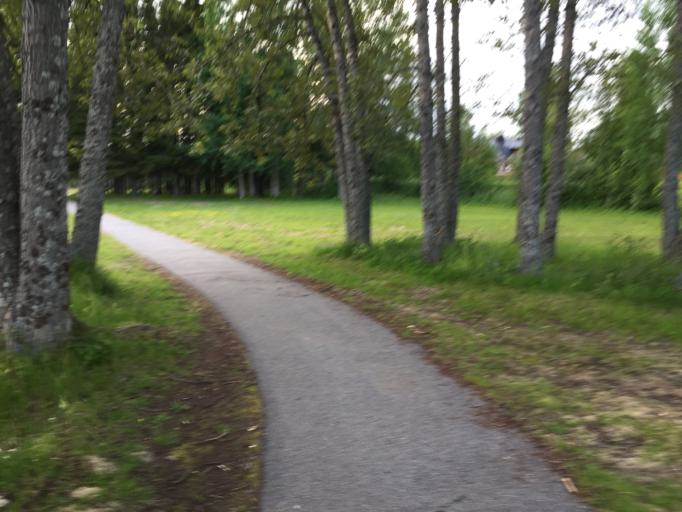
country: SE
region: Vaesterbotten
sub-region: Storumans Kommun
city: Storuman
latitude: 65.1025
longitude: 17.1187
